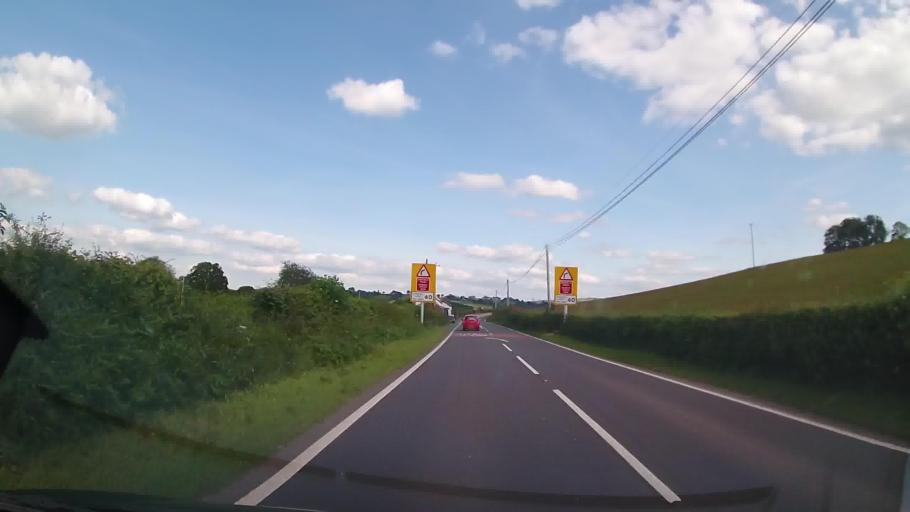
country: GB
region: Wales
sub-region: Sir Powys
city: Llanfyllin
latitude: 52.6653
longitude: -3.3735
